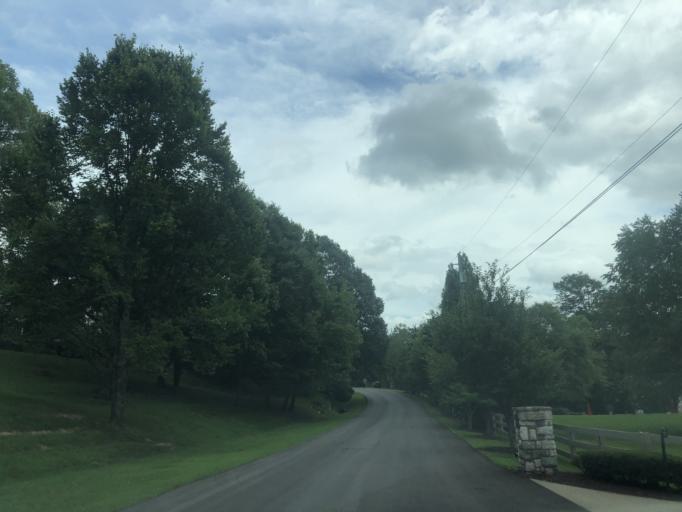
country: US
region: Tennessee
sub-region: Davidson County
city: Forest Hills
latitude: 36.0701
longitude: -86.8143
